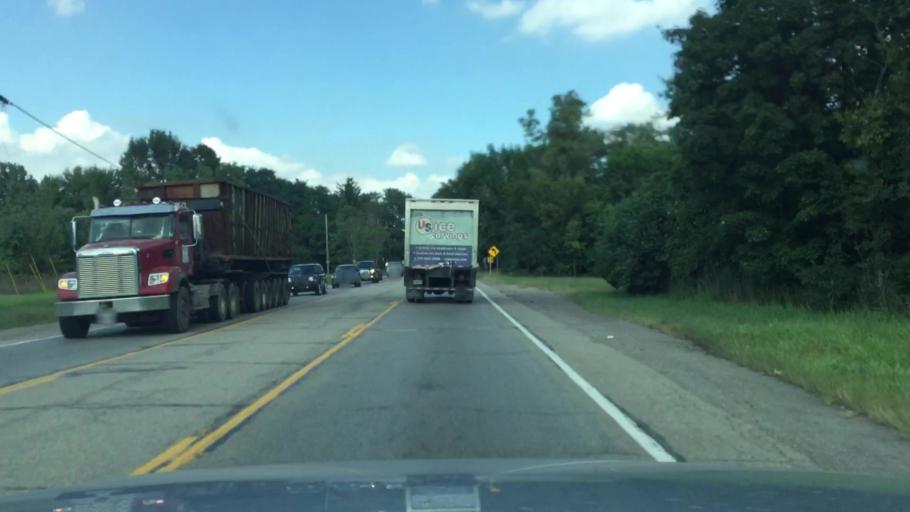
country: US
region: Michigan
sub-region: Wayne County
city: Romulus
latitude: 42.2484
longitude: -83.3864
